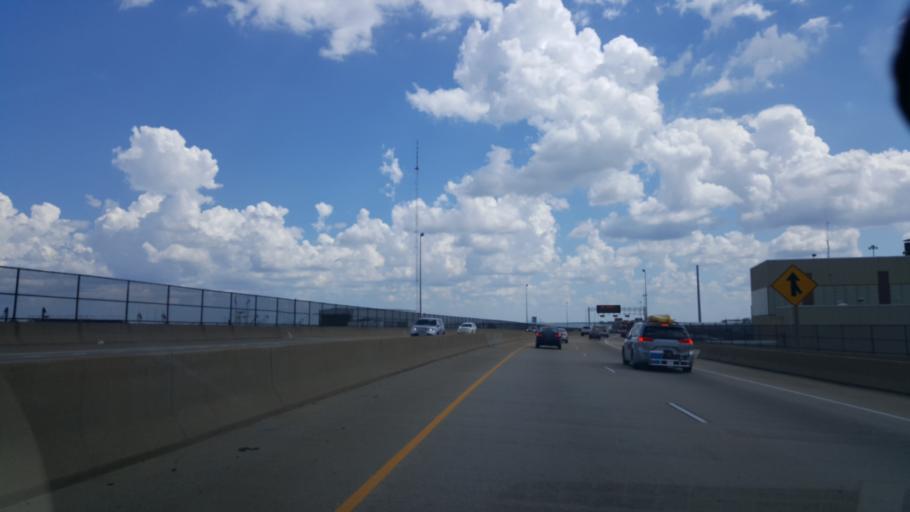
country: US
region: Virginia
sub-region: City of Newport News
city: Newport News
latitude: 36.9666
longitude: -76.4143
